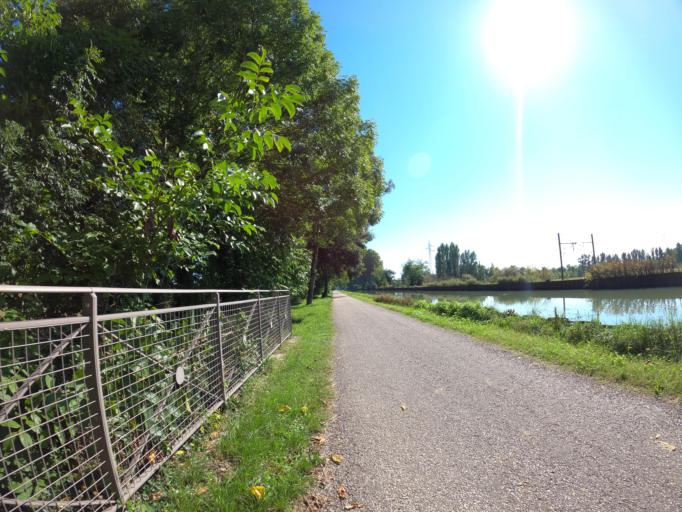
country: FR
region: Aquitaine
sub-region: Departement du Lot-et-Garonne
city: Bon-Encontre
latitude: 44.1731
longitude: 0.6705
